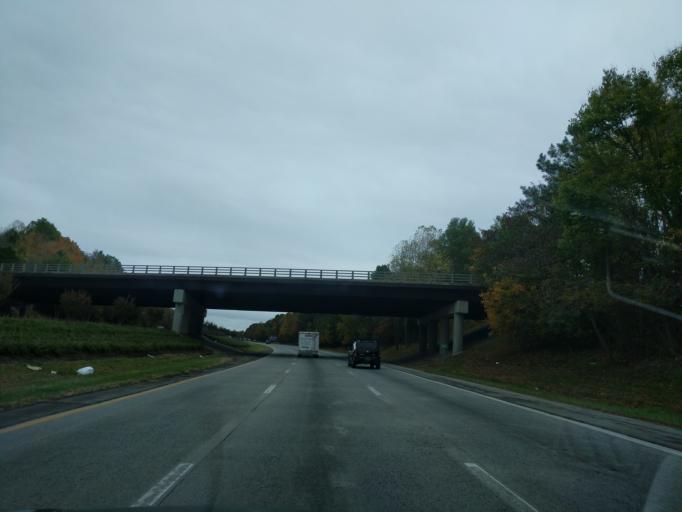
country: US
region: North Carolina
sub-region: Davidson County
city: Thomasville
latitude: 35.8554
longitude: -80.0916
